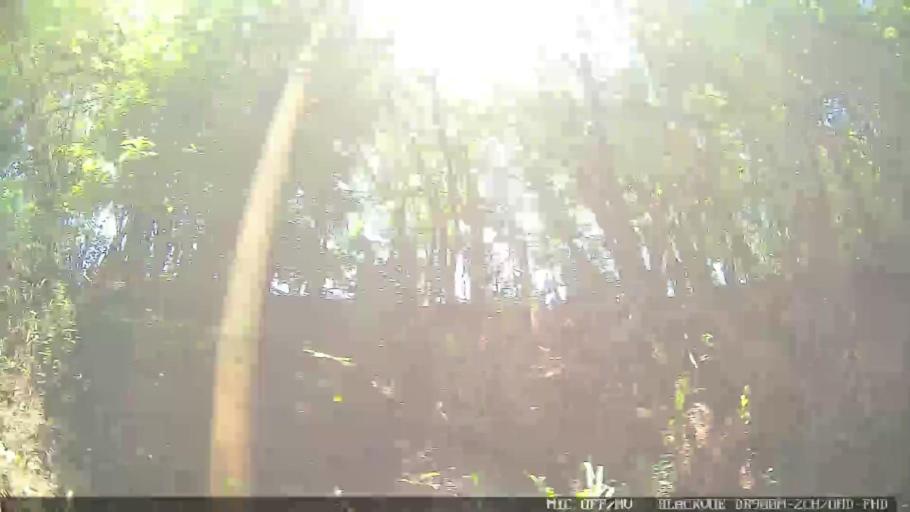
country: BR
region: Sao Paulo
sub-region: Jaguariuna
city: Jaguariuna
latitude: -22.7144
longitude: -46.9872
